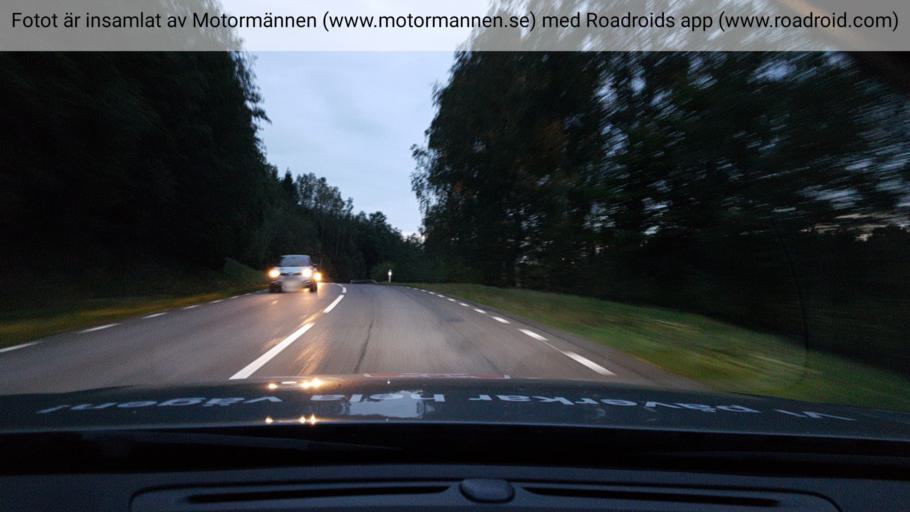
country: SE
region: OErebro
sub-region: Karlskoga Kommun
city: Karlskoga
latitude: 59.4138
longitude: 14.6792
